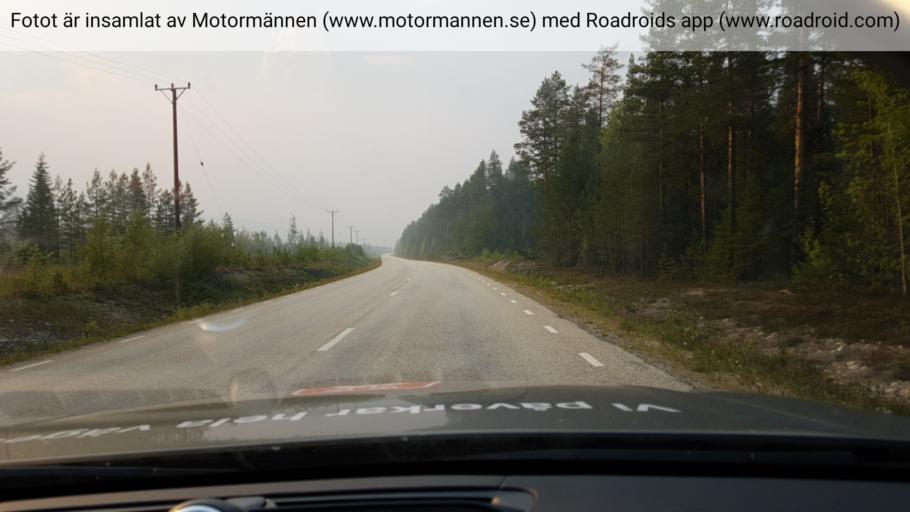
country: SE
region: Jaemtland
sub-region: Bergs Kommun
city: Hoverberg
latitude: 62.4876
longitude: 14.2278
